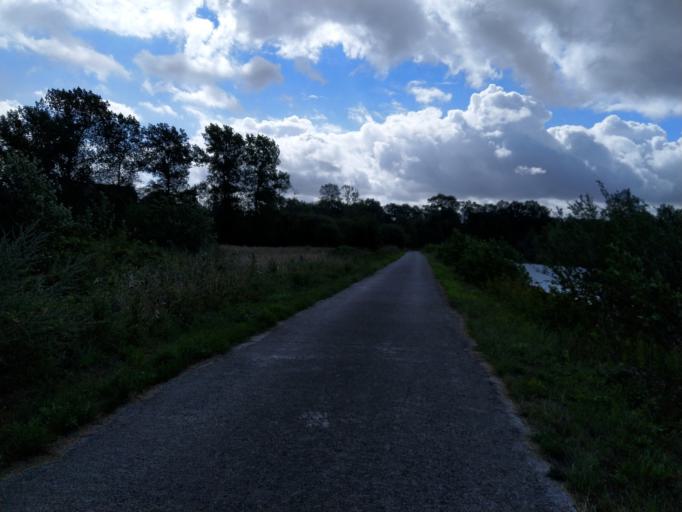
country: BE
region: Wallonia
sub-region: Province du Hainaut
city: Merbes-le-Chateau
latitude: 50.3257
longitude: 4.2166
